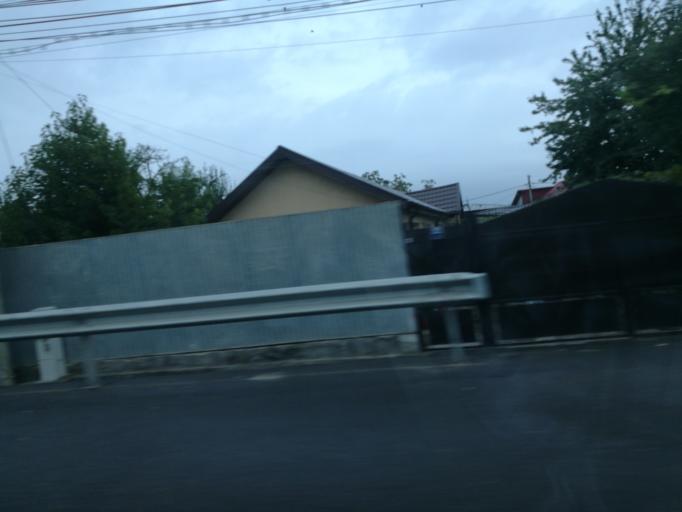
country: RO
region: Galati
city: Galati
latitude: 45.4677
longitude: 28.0345
